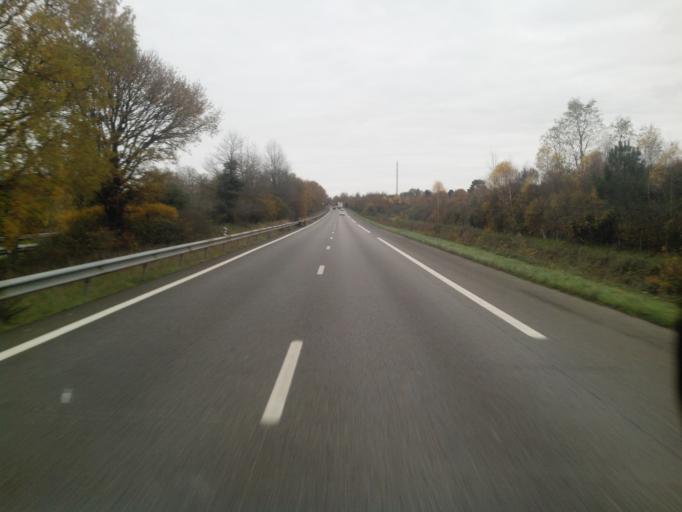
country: FR
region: Pays de la Loire
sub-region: Departement de la Loire-Atlantique
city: Heric
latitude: 47.4065
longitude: -1.6430
